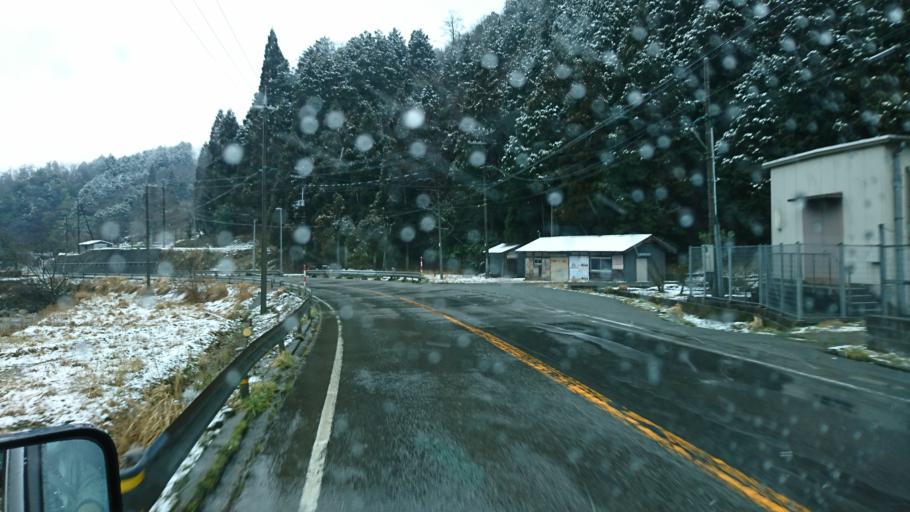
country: JP
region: Tottori
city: Tottori
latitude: 35.5426
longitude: 134.5064
